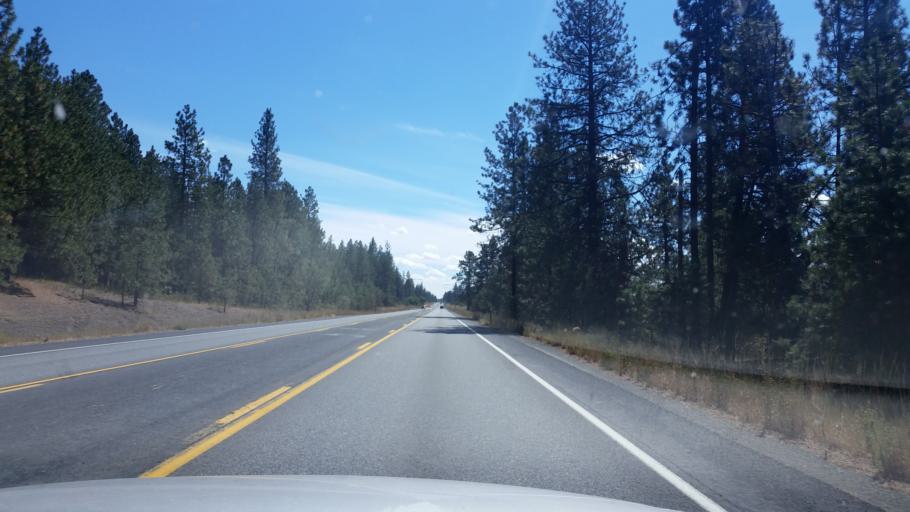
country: US
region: Washington
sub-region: Spokane County
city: Cheney
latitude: 47.5523
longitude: -117.5914
